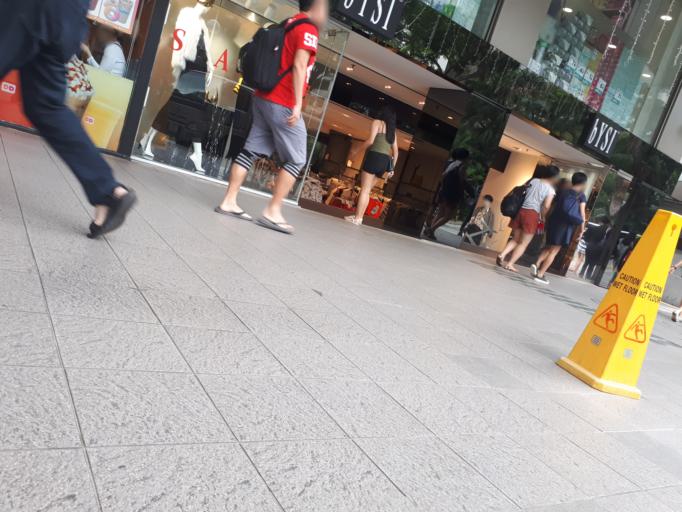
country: SG
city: Singapore
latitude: 1.3070
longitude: 103.8332
